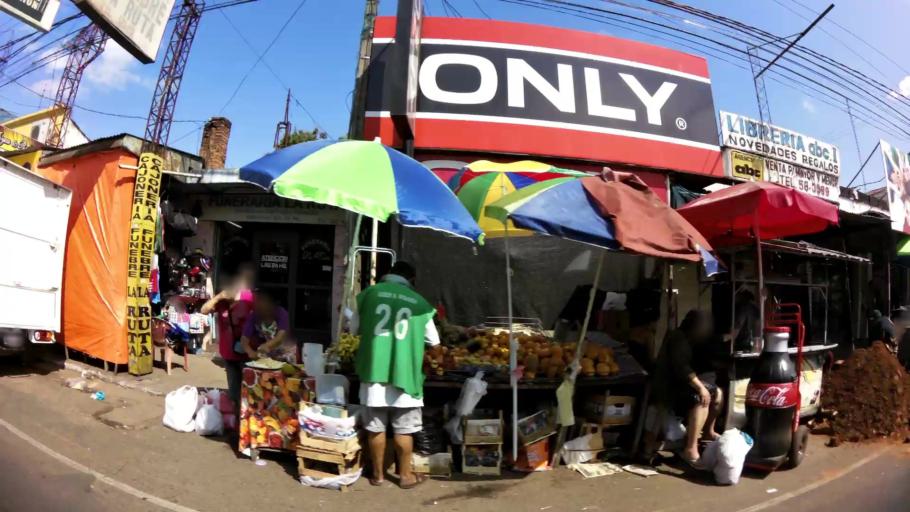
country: PY
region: Central
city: San Lorenzo
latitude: -25.3461
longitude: -57.5096
